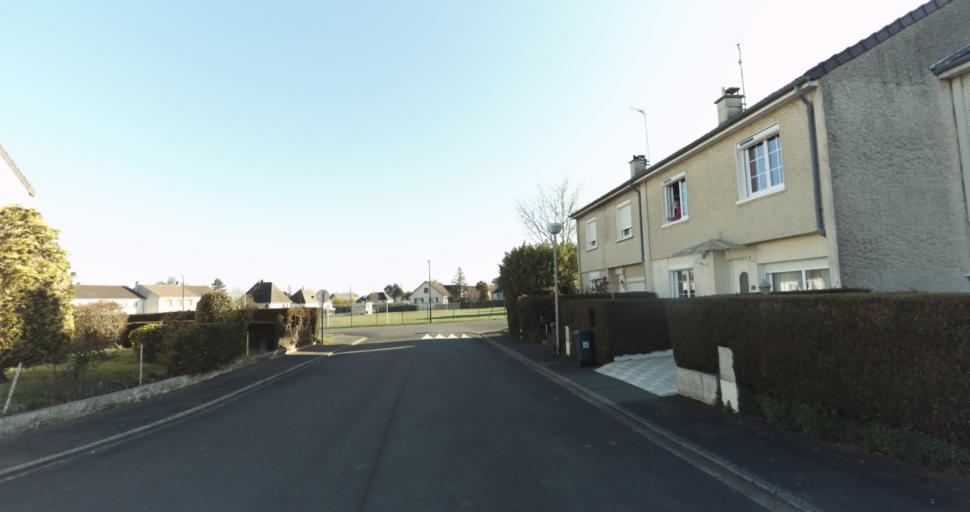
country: FR
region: Lower Normandy
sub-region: Departement du Calvados
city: Saint-Pierre-sur-Dives
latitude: 49.0220
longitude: -0.0267
